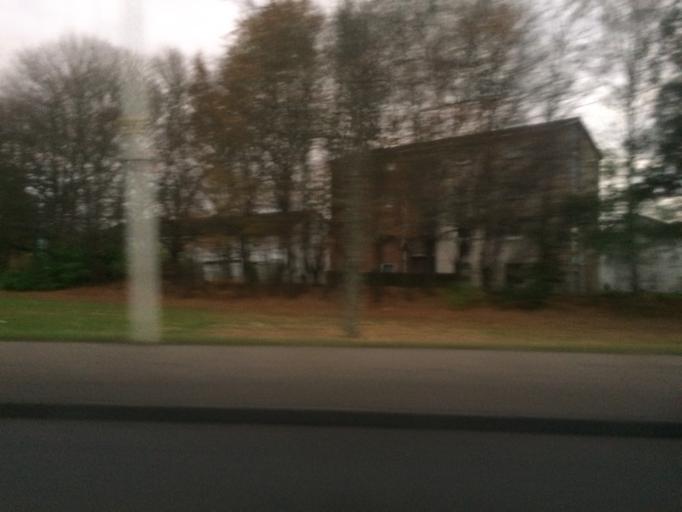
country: GB
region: Scotland
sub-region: Perth and Kinross
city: Perth
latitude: 56.4119
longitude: -3.4548
